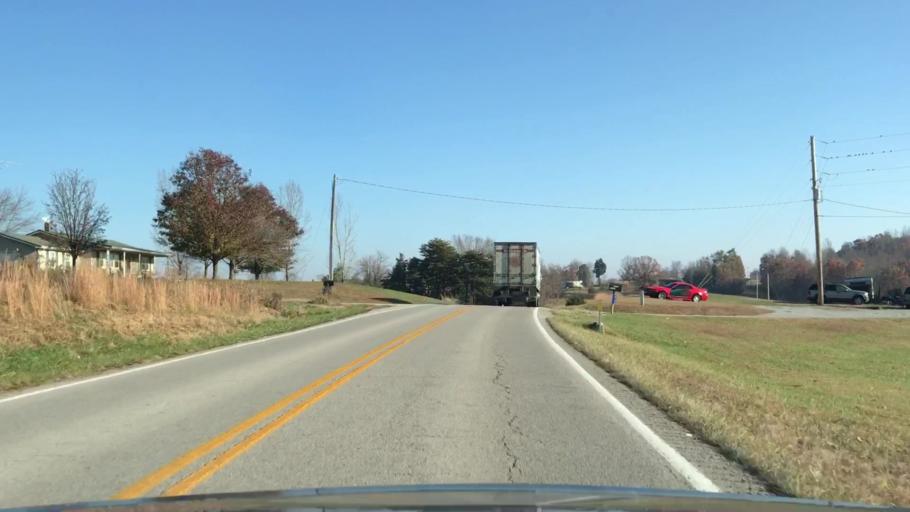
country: US
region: Kentucky
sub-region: Grayson County
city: Leitchfield
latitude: 37.3852
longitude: -86.2520
